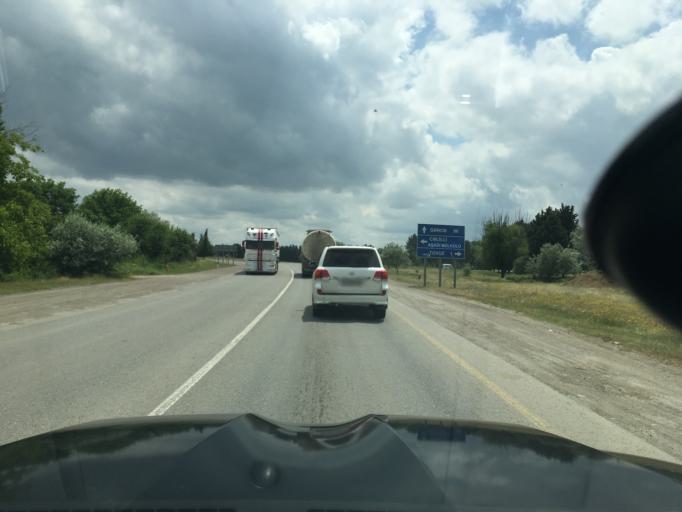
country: AZ
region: Tovuz
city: Qaraxanli
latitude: 41.0305
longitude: 45.5966
